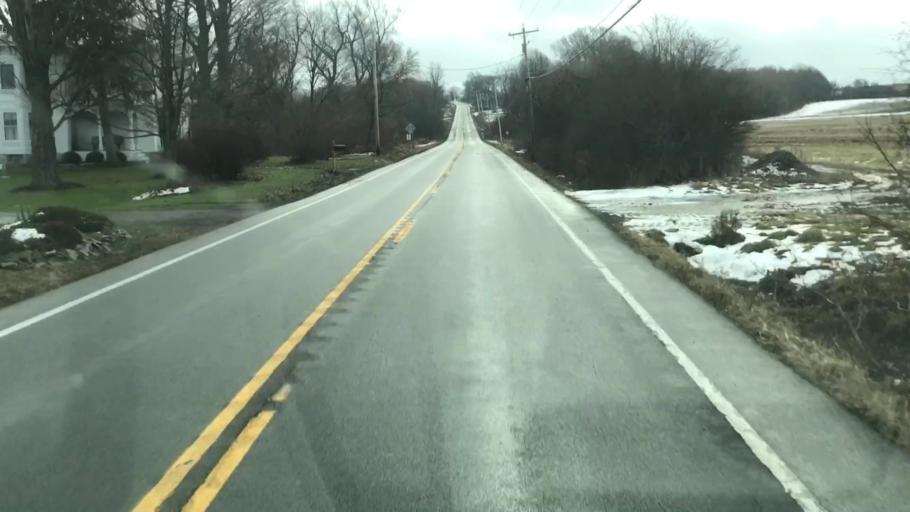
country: US
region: New York
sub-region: Onondaga County
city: Skaneateles
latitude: 42.8533
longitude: -76.3950
